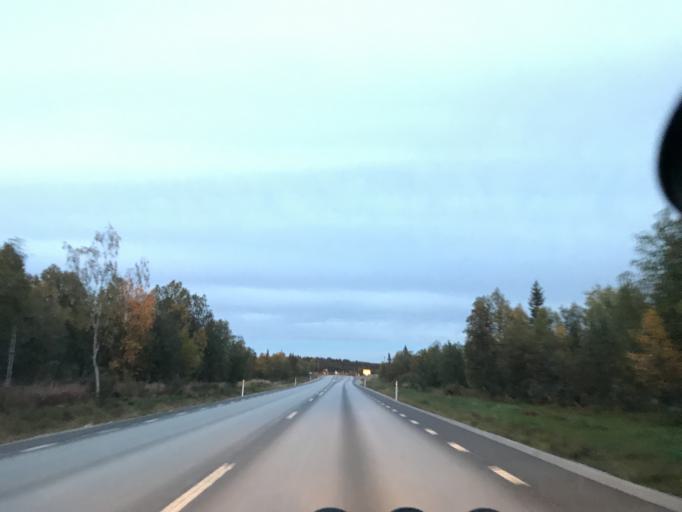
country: SE
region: Norrbotten
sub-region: Gallivare Kommun
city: Malmberget
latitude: 67.6462
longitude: 21.0335
